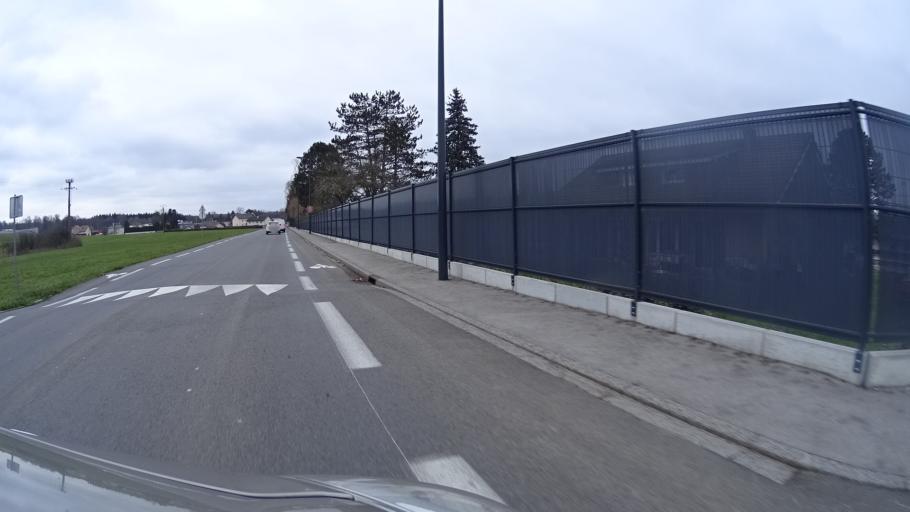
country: FR
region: Franche-Comte
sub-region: Departement du Doubs
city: Saone
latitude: 47.2123
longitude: 6.1055
